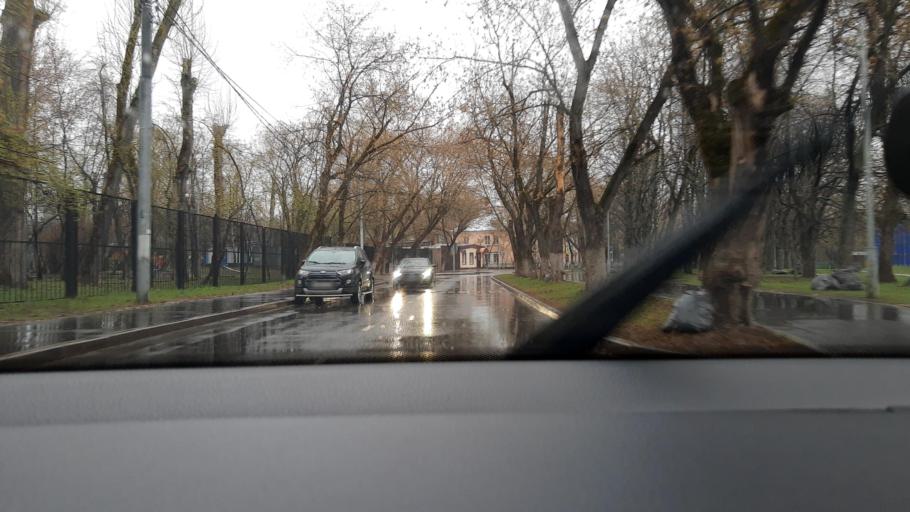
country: RU
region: Moskovskaya
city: Kur'yanovo
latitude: 55.6568
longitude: 37.6979
